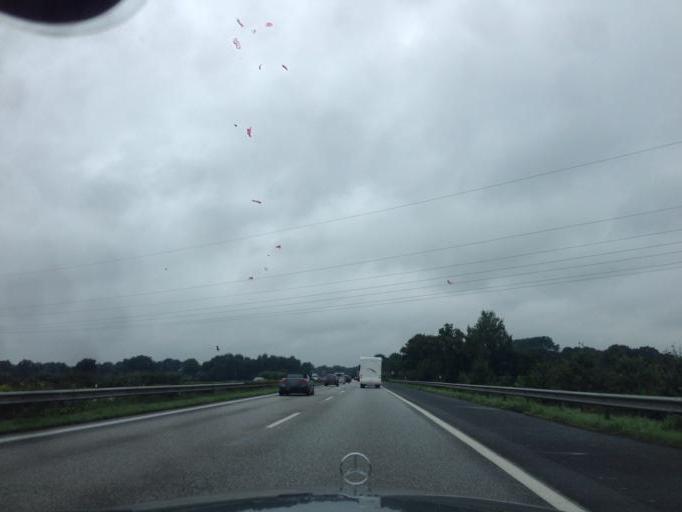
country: DE
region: Schleswig-Holstein
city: Schmalfeld
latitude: 53.8672
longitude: 9.9469
